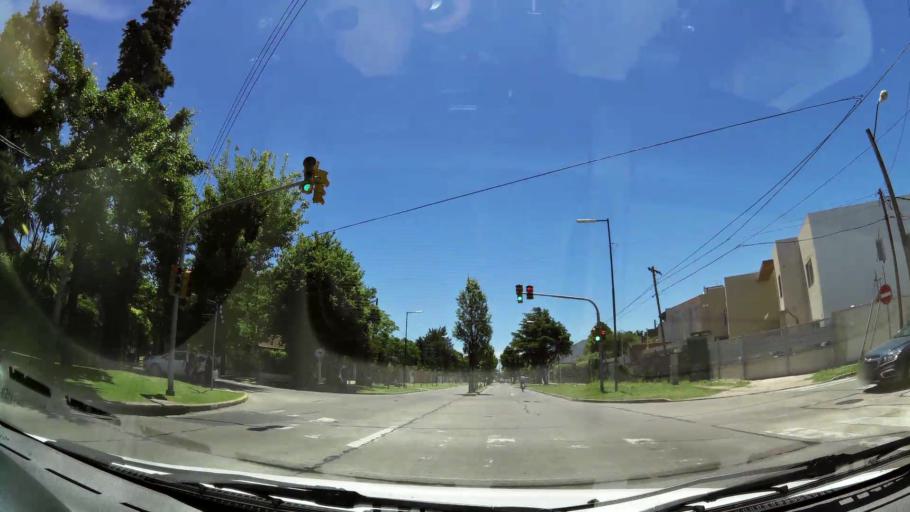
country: AR
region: Buenos Aires
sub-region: Partido de San Isidro
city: San Isidro
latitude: -34.4996
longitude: -58.5601
